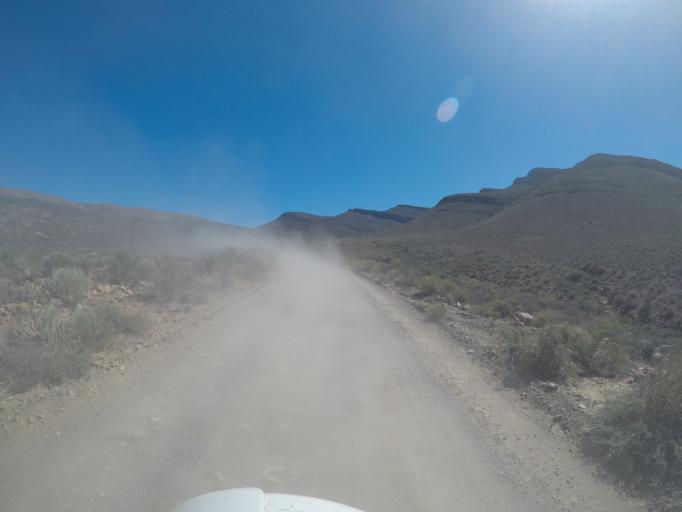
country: ZA
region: Western Cape
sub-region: West Coast District Municipality
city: Clanwilliam
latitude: -32.6302
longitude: 19.3946
